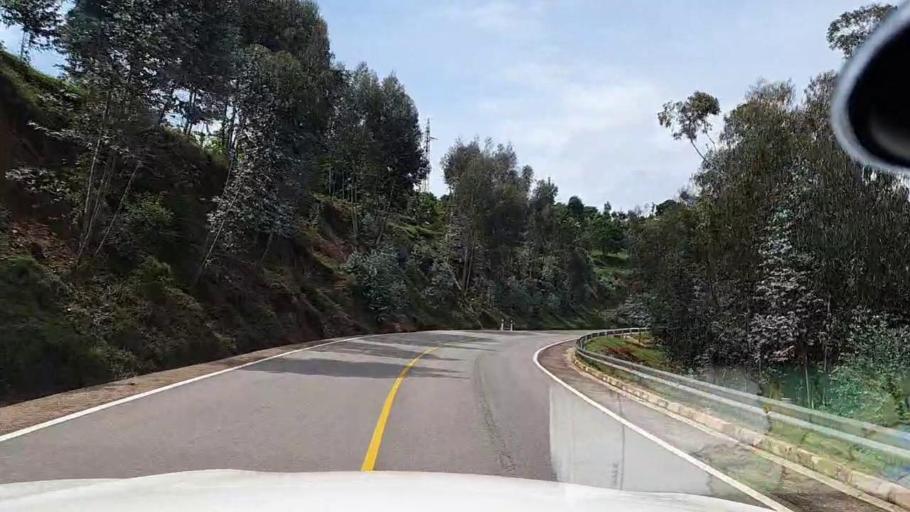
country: RW
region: Southern Province
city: Nzega
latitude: -2.5065
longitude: 29.5010
